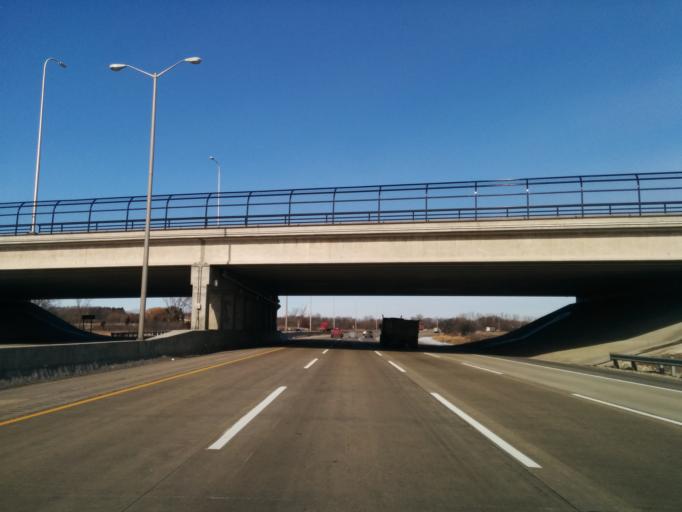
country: US
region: Illinois
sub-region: Lake County
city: Wadsworth
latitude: 42.4649
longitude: -87.9634
